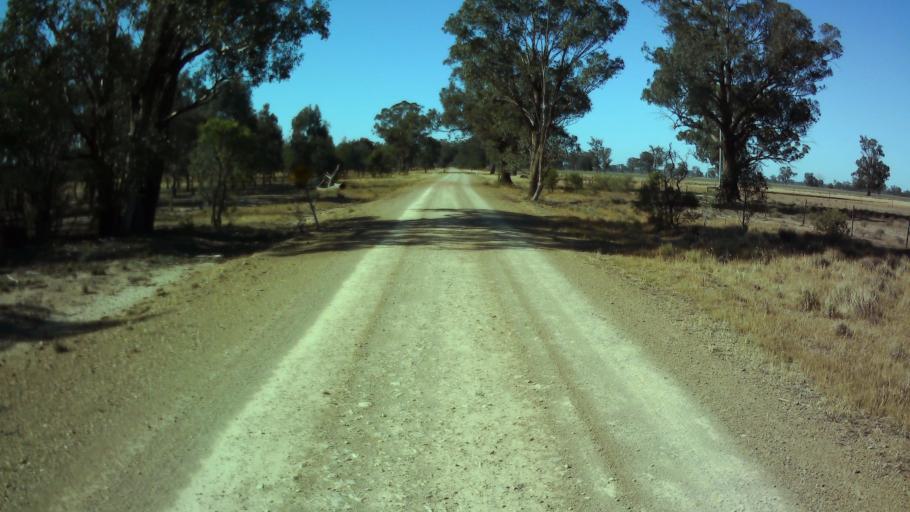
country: AU
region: New South Wales
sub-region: Weddin
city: Grenfell
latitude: -33.9308
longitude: 147.8729
